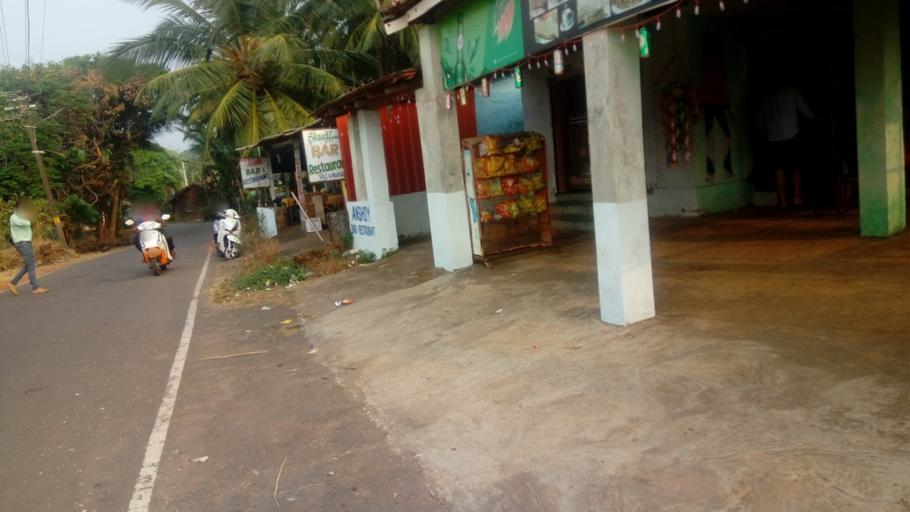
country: IN
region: Goa
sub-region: South Goa
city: Cavelossim
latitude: 15.0981
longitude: 73.9317
